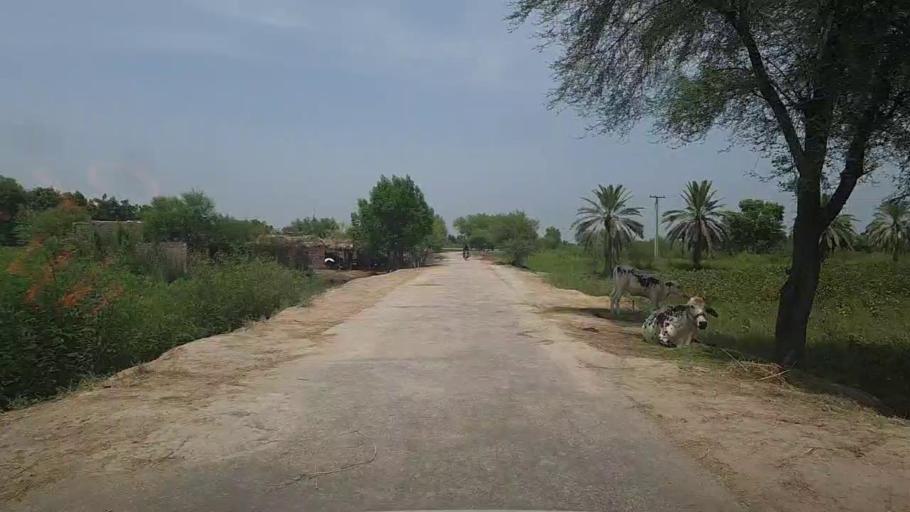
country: PK
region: Sindh
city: Ubauro
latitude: 28.1889
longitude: 69.7702
